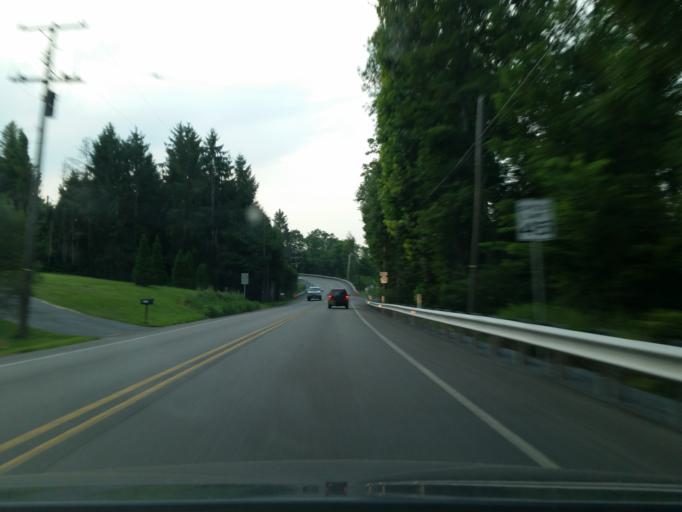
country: US
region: Pennsylvania
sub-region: Lebanon County
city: Jonestown
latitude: 40.3892
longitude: -76.4785
